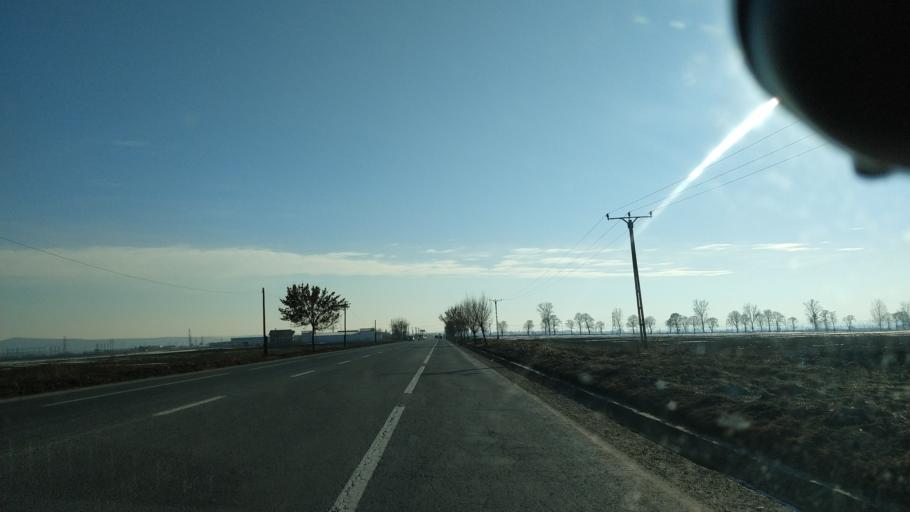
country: RO
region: Neamt
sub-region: Comuna Sabaoani
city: Traian
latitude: 46.9745
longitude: 26.9088
